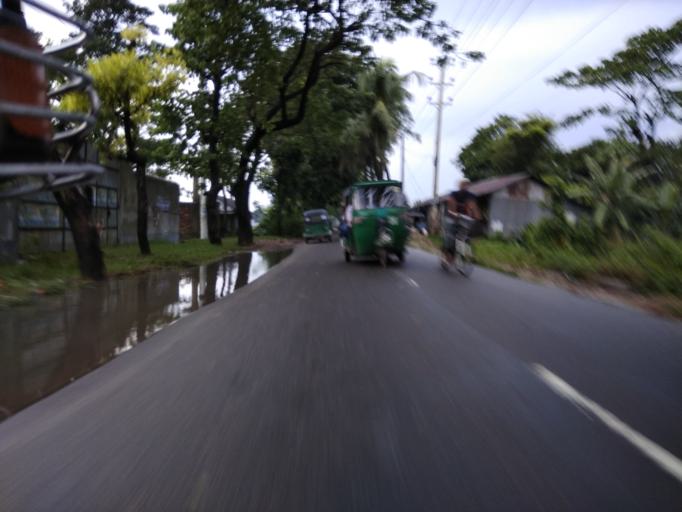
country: BD
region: Dhaka
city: Azimpur
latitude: 23.6979
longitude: 90.3416
